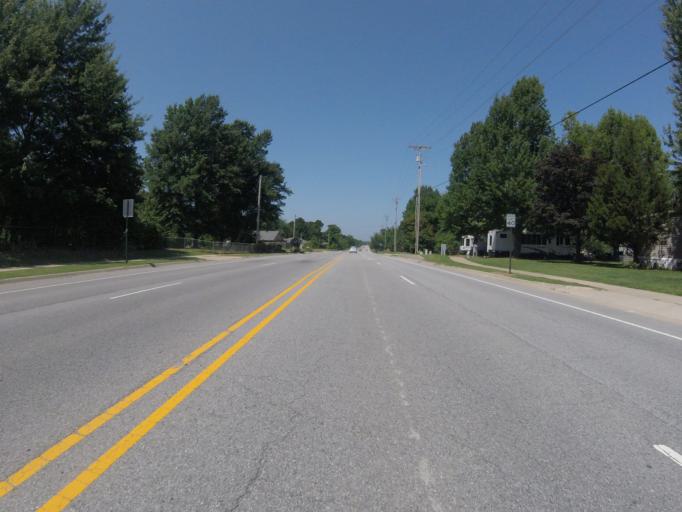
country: US
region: Arkansas
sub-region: Washington County
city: Fayetteville
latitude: 36.0926
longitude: -94.1951
